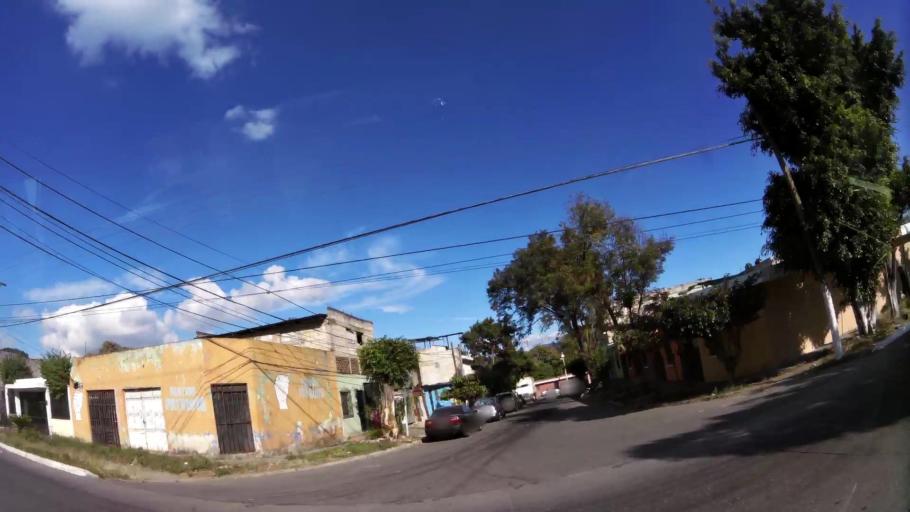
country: GT
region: Guatemala
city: Villa Nueva
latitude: 14.5203
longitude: -90.5745
